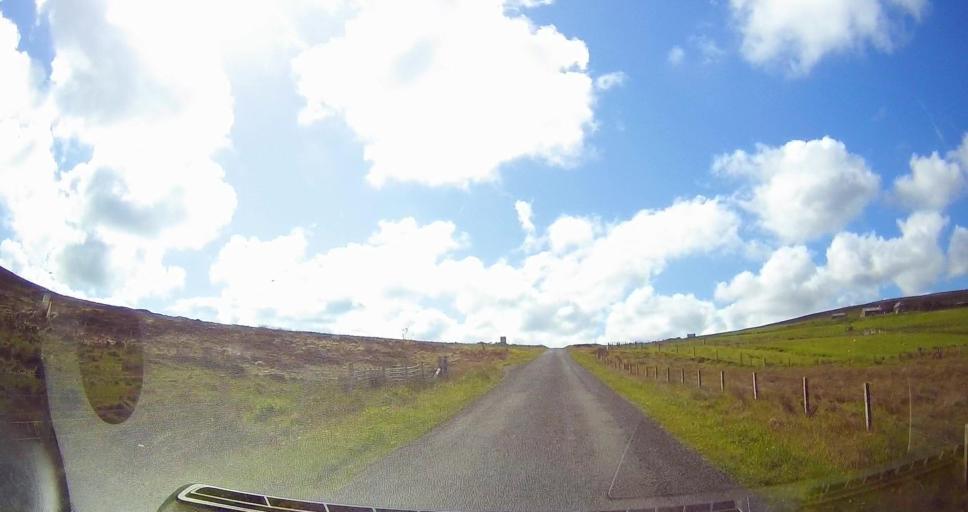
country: GB
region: Scotland
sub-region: Orkney Islands
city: Orkney
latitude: 59.0496
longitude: -3.1135
